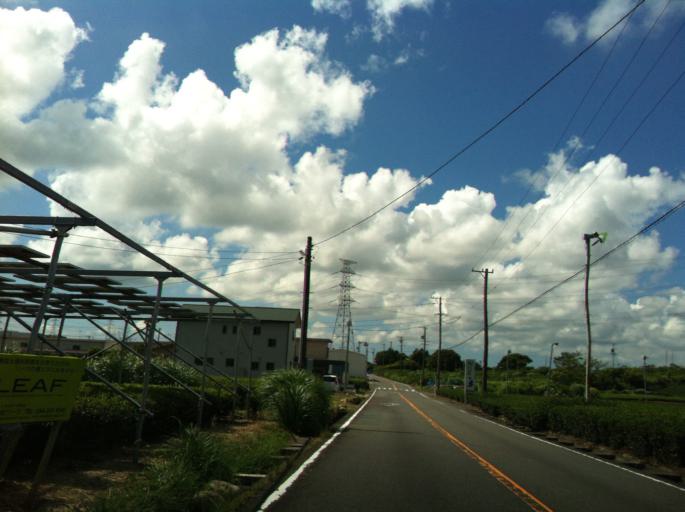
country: JP
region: Shizuoka
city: Kanaya
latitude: 34.7832
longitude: 138.1358
